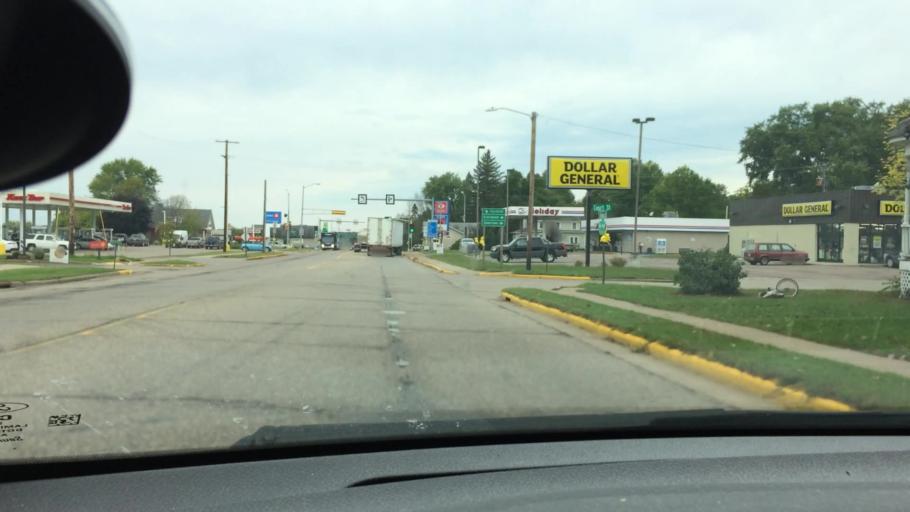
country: US
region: Wisconsin
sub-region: Clark County
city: Neillsville
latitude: 44.5527
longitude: -90.5944
